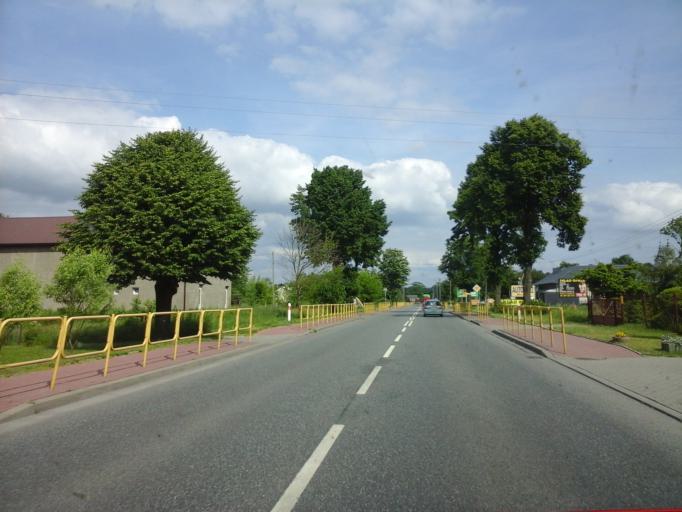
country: PL
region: Lodz Voivodeship
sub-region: Powiat opoczynski
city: Paradyz
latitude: 51.3069
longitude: 20.1080
